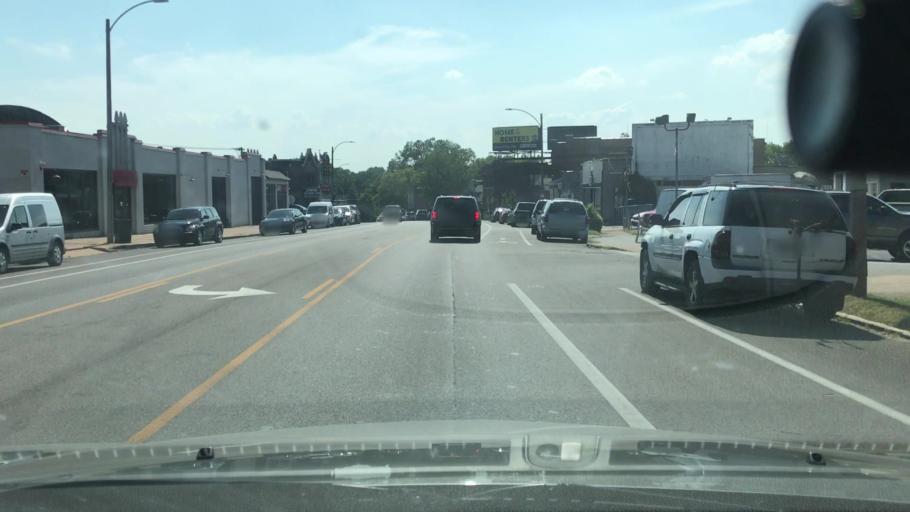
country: US
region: Missouri
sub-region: Saint Louis County
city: Lemay
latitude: 38.5776
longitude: -90.2733
